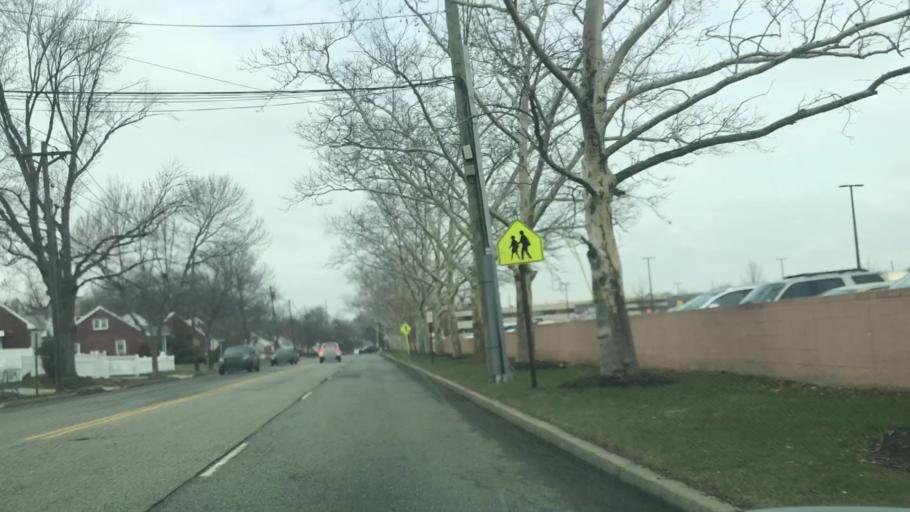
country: US
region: New Jersey
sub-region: Bergen County
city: Maywood
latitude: 40.9143
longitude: -74.0607
